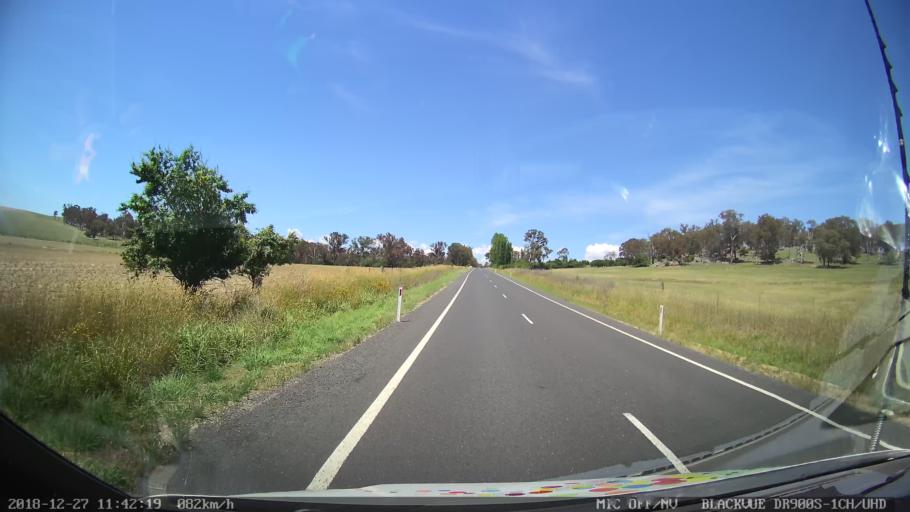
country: AU
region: New South Wales
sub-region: Bathurst Regional
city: Perthville
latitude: -33.5472
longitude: 149.4788
